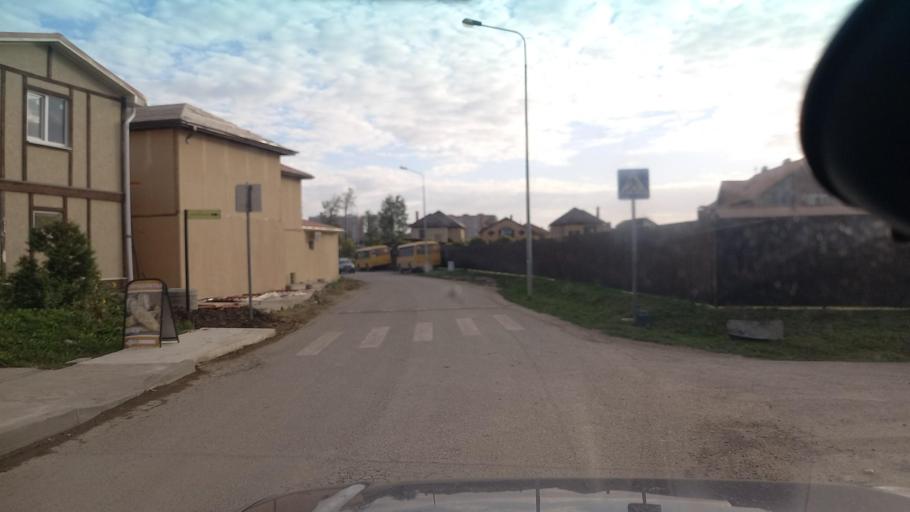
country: RU
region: Krasnodarskiy
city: Krasnodar
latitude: 45.1215
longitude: 38.9229
